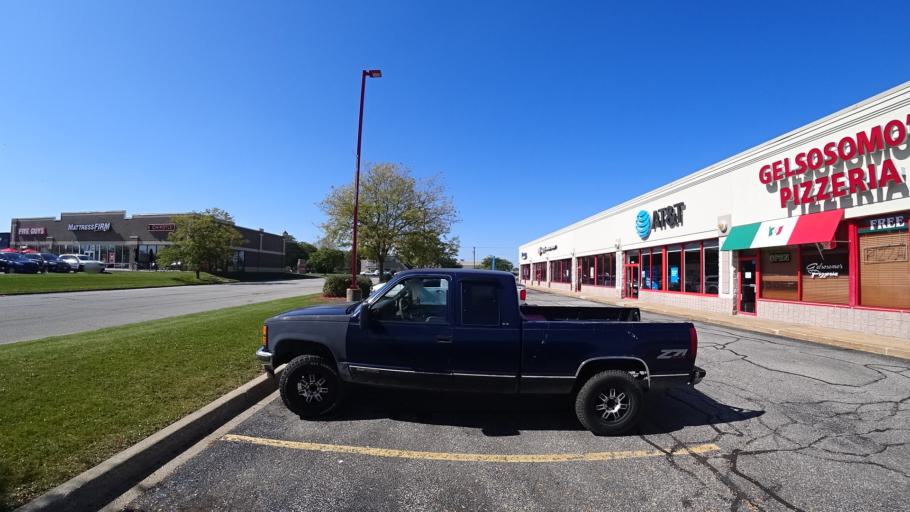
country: US
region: Indiana
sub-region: LaPorte County
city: Michigan City
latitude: 41.6737
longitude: -86.8928
